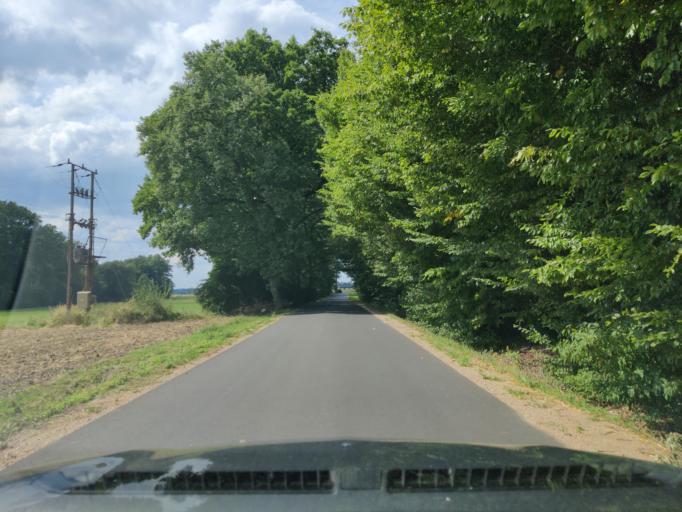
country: PL
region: Masovian Voivodeship
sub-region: Powiat pultuski
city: Obryte
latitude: 52.6913
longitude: 21.2129
